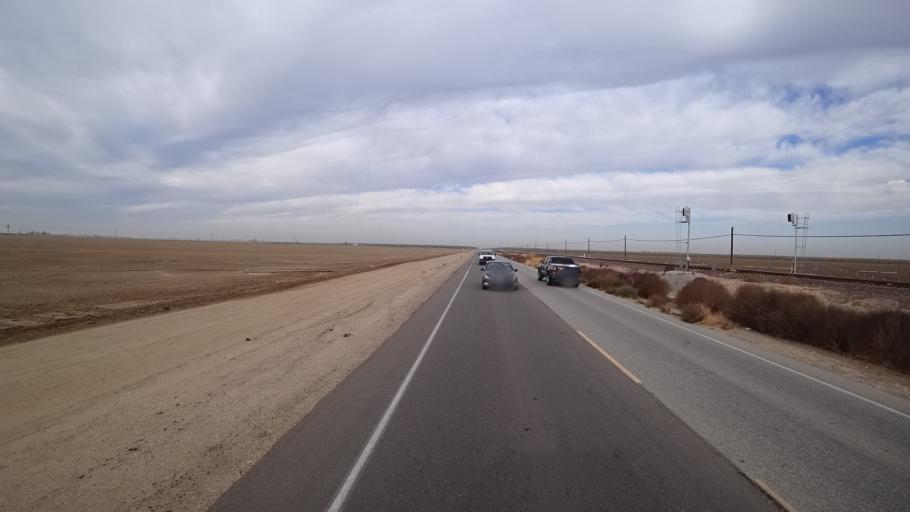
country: US
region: California
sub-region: Kern County
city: Rosedale
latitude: 35.4150
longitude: -119.1667
